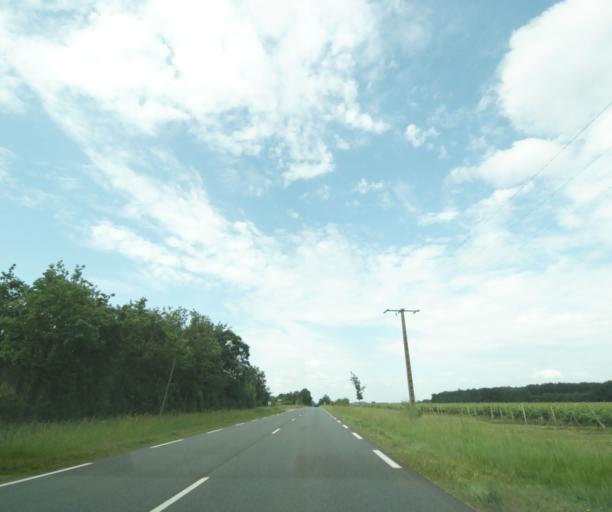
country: FR
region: Pays de la Loire
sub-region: Departement de Maine-et-Loire
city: Montreuil-Bellay
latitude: 47.1537
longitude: -0.1475
